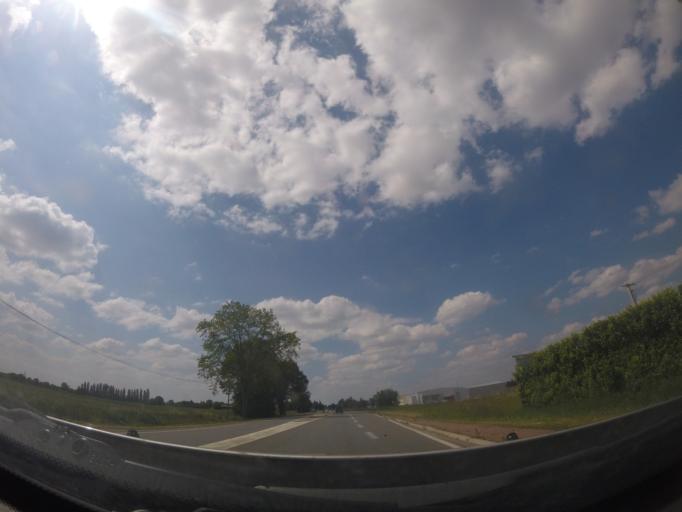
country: FR
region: Poitou-Charentes
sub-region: Departement de la Charente-Maritime
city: Bords
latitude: 45.8531
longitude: -0.8264
